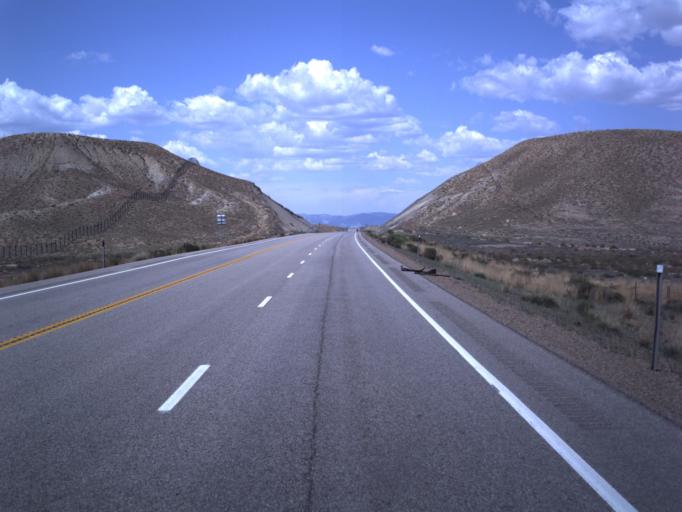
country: US
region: Utah
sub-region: Carbon County
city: Price
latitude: 39.4639
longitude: -110.8587
